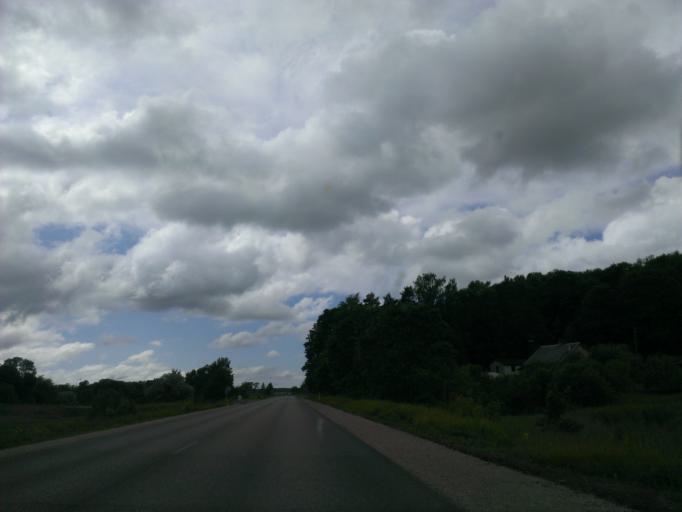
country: LV
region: Durbe
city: Liegi
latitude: 56.5915
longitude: 21.3778
